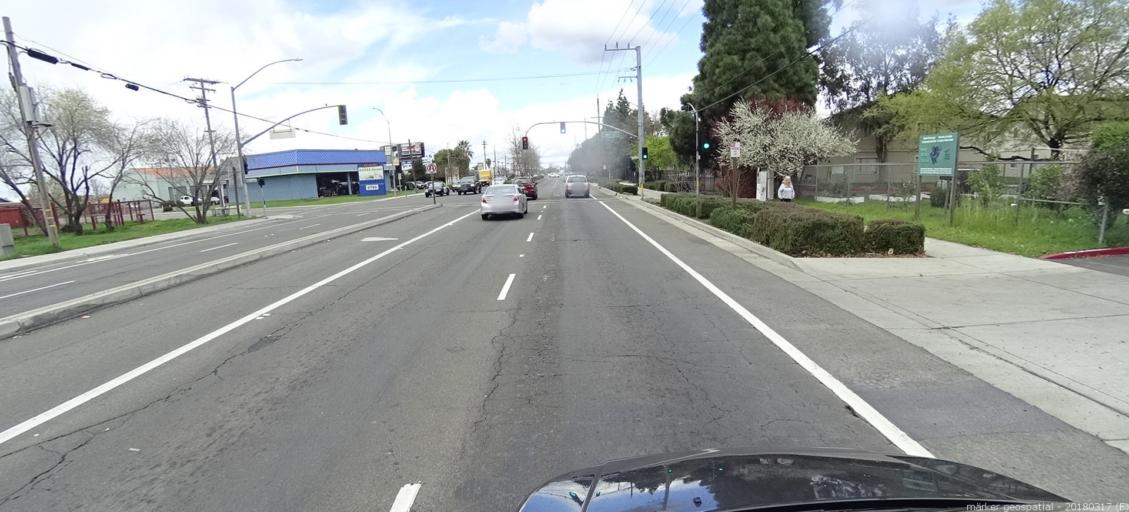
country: US
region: California
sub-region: Sacramento County
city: Parkway
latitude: 38.5027
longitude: -121.4628
